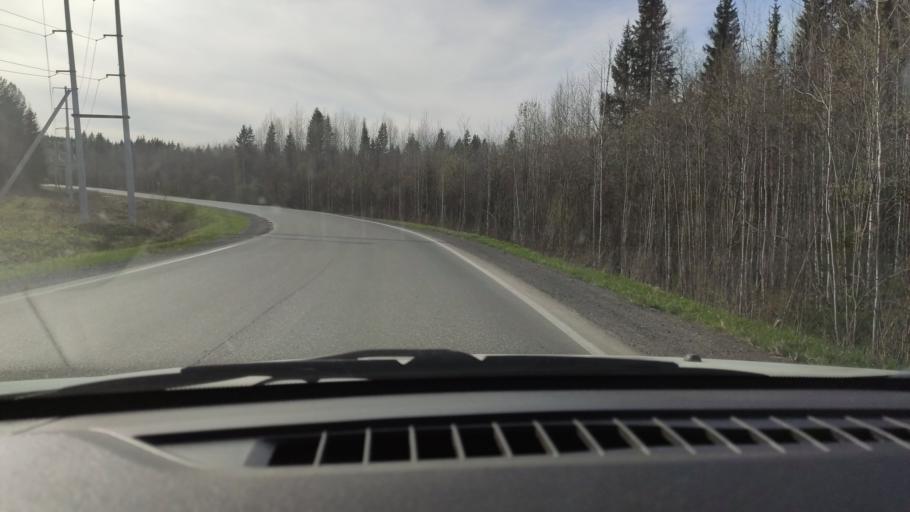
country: RU
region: Perm
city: Novyye Lyady
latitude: 57.9598
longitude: 56.5459
